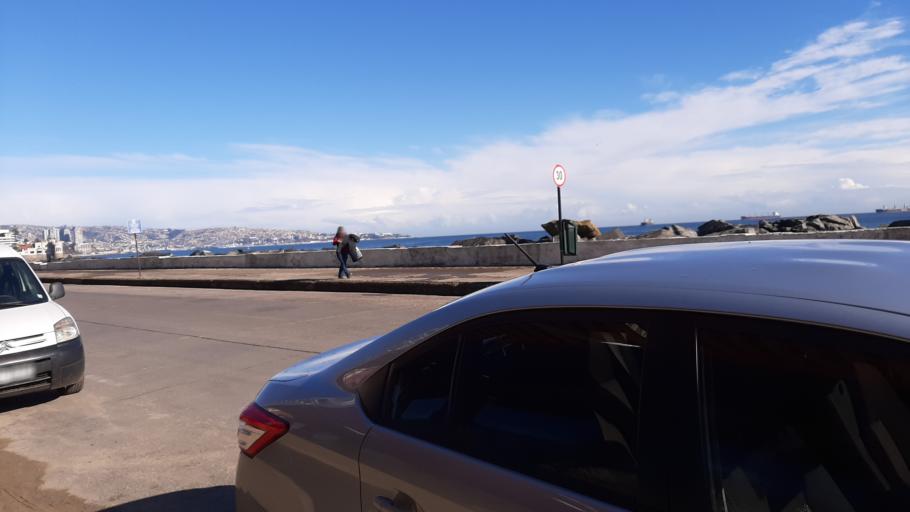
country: CL
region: Valparaiso
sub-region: Provincia de Valparaiso
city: Vina del Mar
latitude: -33.0164
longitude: -71.5586
